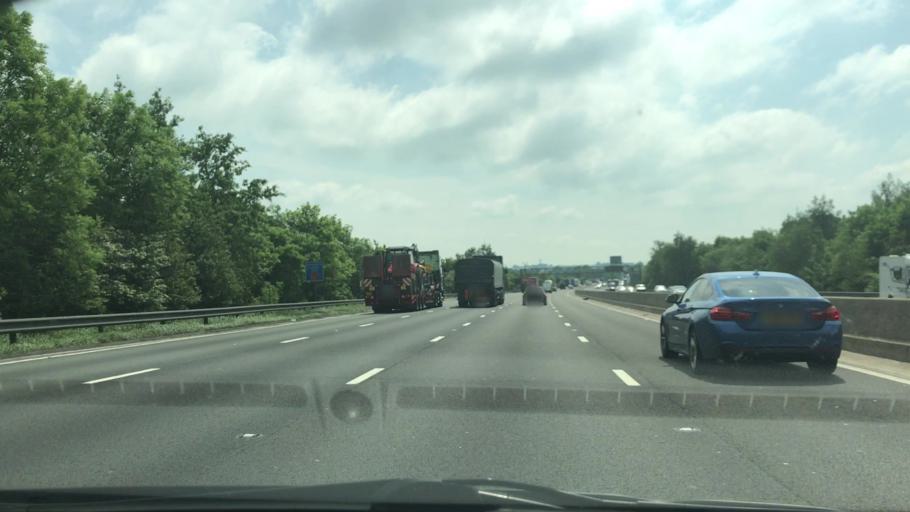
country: GB
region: England
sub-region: Derbyshire
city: Tibshelf
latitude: 53.1854
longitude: -1.3229
